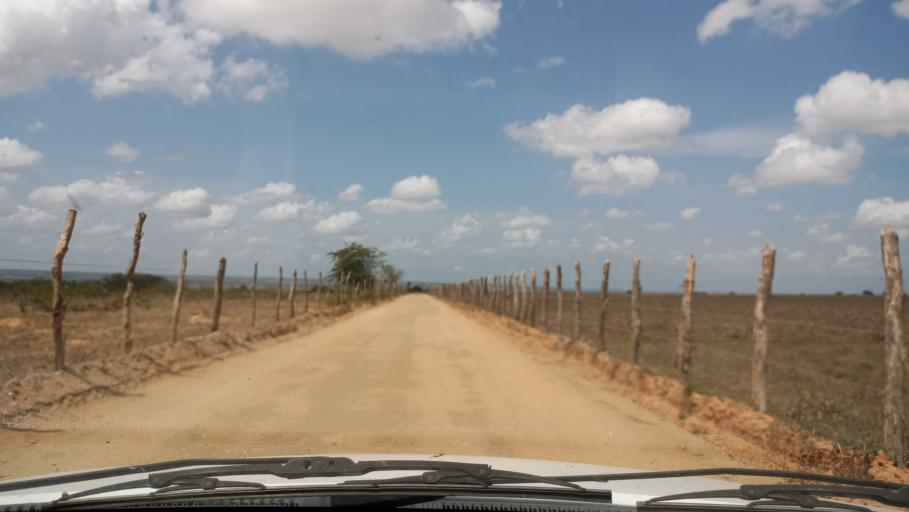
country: BR
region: Rio Grande do Norte
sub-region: Montanhas
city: Montanhas
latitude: -6.3521
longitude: -35.3336
